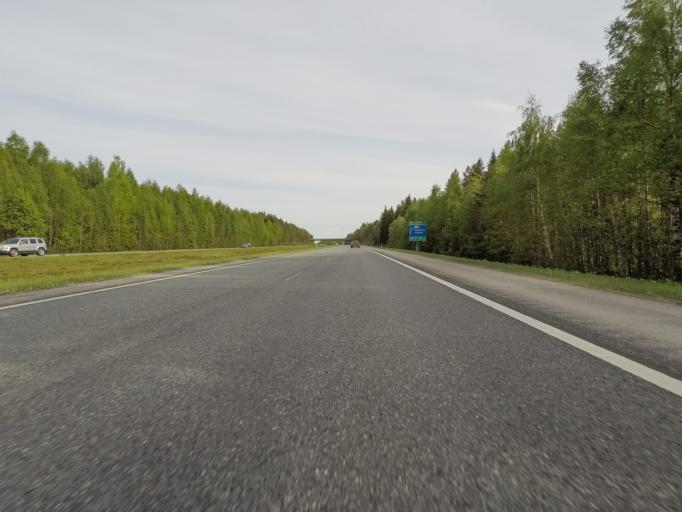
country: FI
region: Haeme
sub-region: Haemeenlinna
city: Janakkala
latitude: 60.9226
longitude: 24.5266
